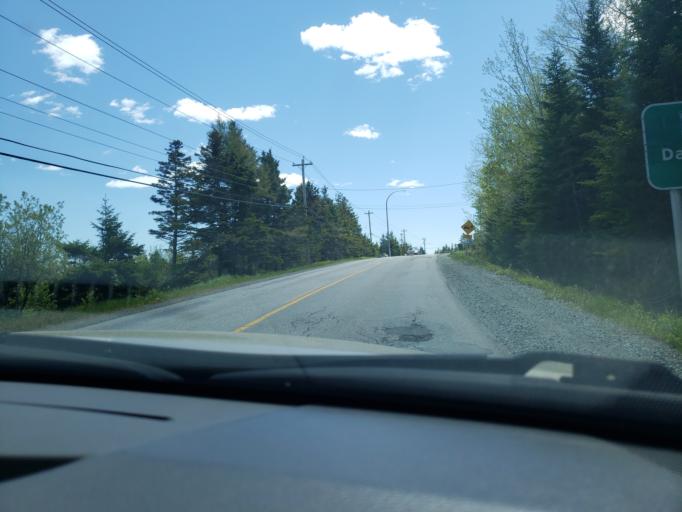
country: CA
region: Nova Scotia
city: Cole Harbour
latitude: 44.7272
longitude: -63.3066
